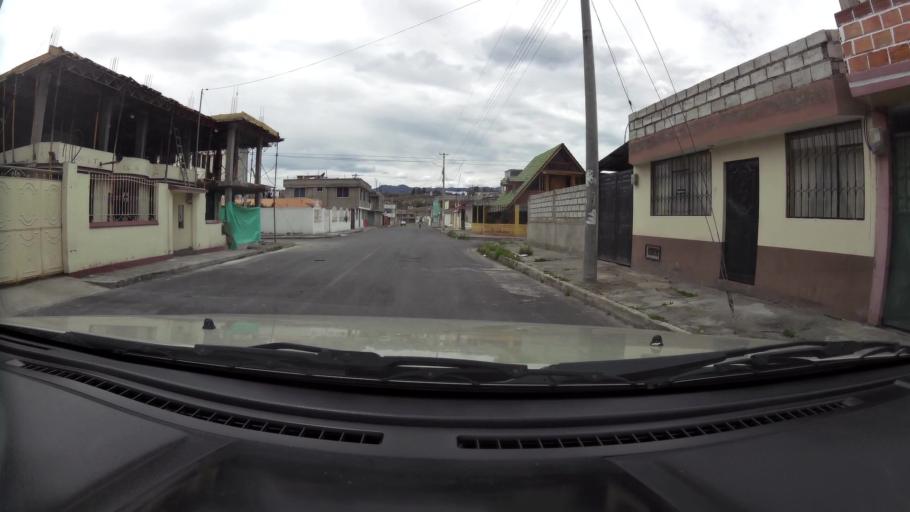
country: EC
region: Cotopaxi
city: Latacunga
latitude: -0.9547
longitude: -78.6038
